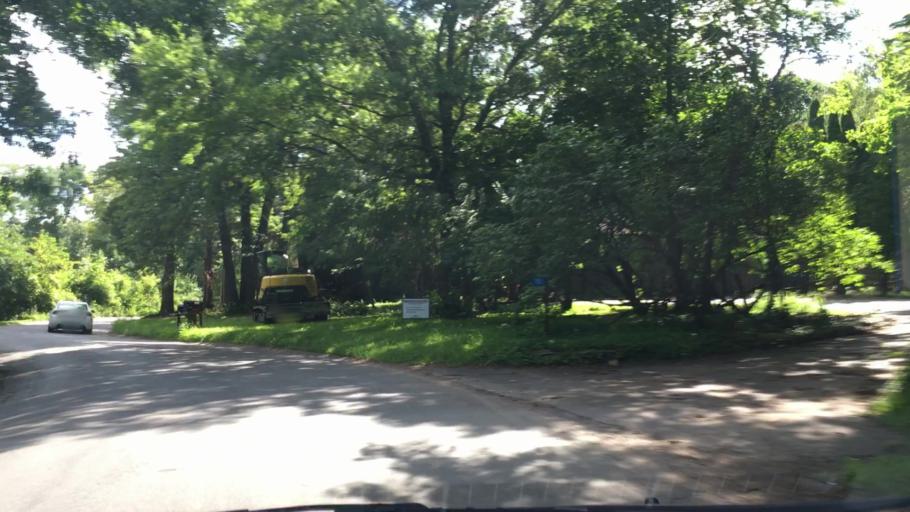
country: US
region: Iowa
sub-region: Johnson County
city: Iowa City
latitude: 41.6891
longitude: -91.5318
